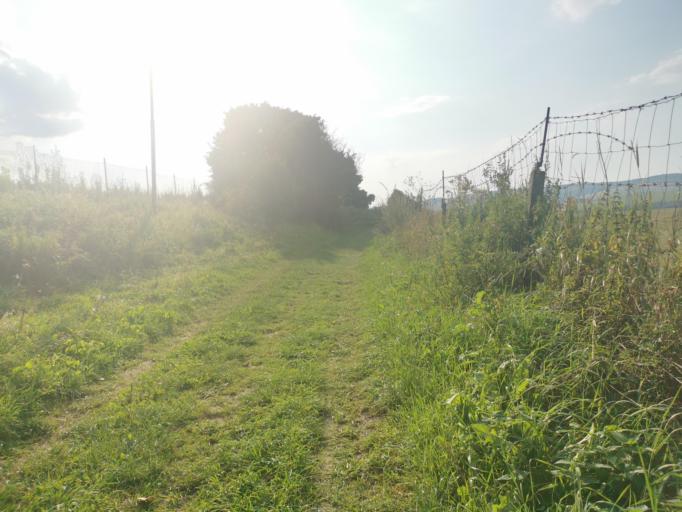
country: SK
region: Trenciansky
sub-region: Okres Myjava
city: Myjava
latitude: 48.7728
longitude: 17.5964
